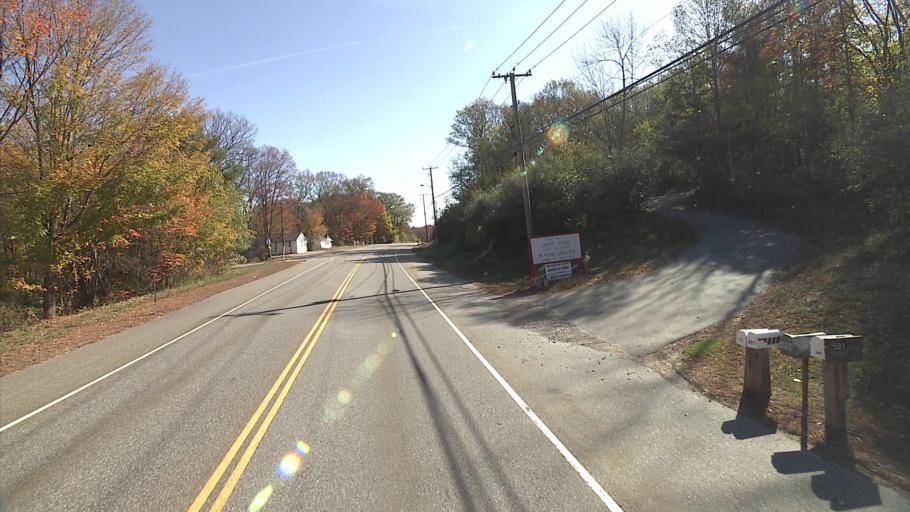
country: US
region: Connecticut
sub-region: Windham County
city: Wauregan
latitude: 41.7851
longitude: -71.9934
